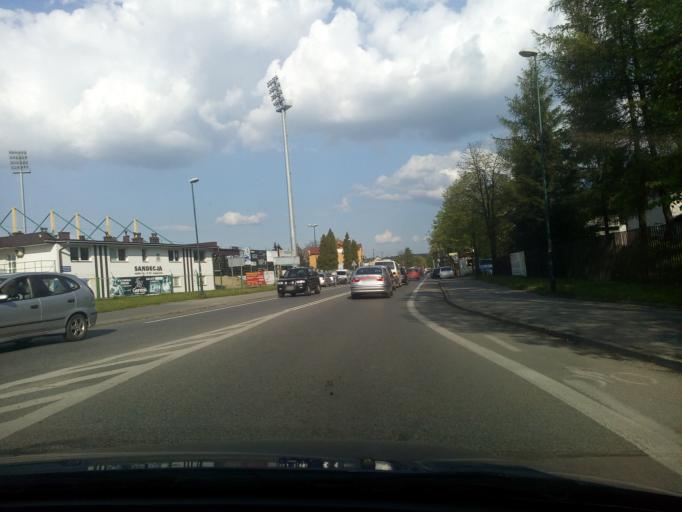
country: PL
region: Lesser Poland Voivodeship
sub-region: Powiat nowosadecki
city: Nowy Sacz
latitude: 49.6203
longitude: 20.7030
